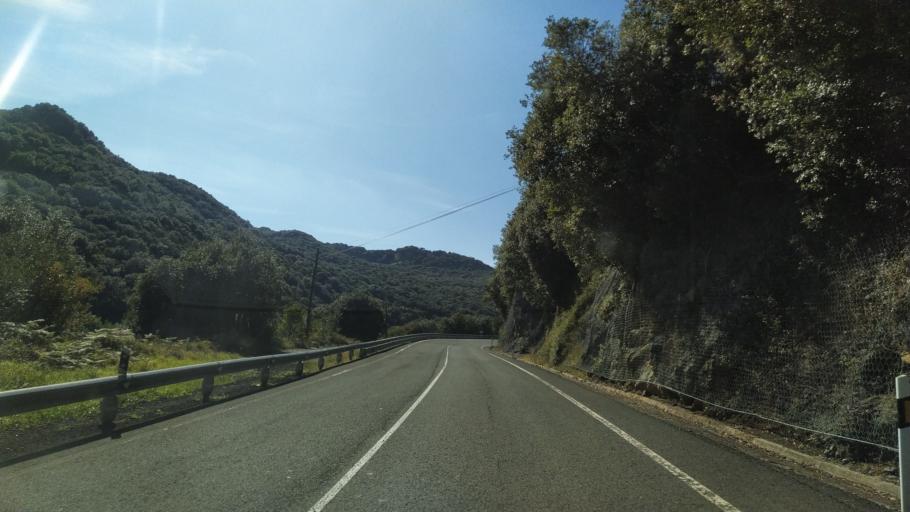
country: ES
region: Cantabria
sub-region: Provincia de Cantabria
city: Liendo
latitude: 43.3914
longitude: -3.3386
